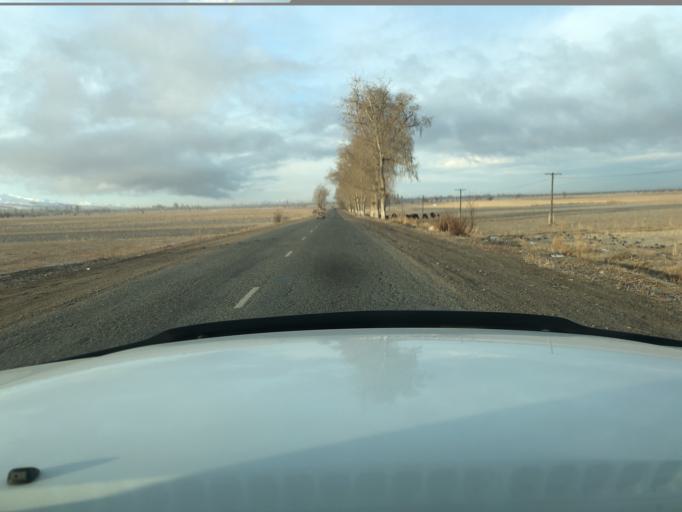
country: KG
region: Ysyk-Koel
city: Karakol
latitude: 42.4765
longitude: 78.3250
